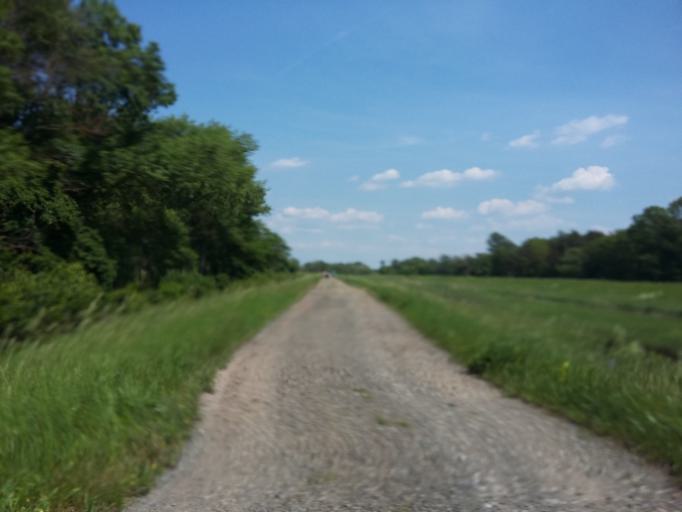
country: AT
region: Lower Austria
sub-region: Politischer Bezirk Ganserndorf
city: Drosing
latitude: 48.4987
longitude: 16.9321
